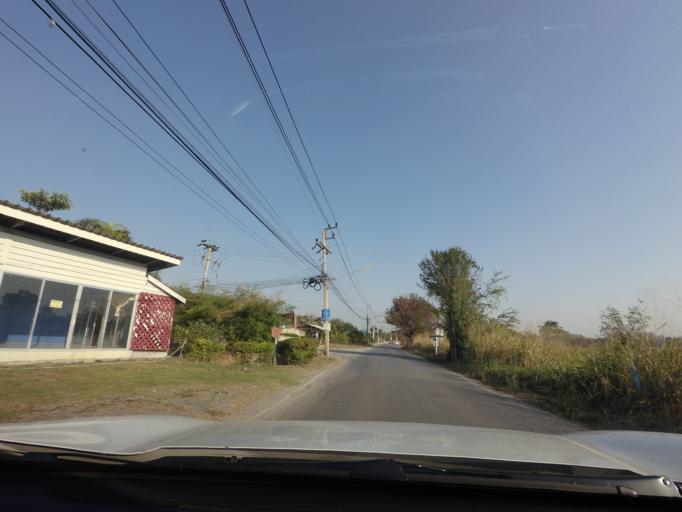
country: TH
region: Nakhon Ratchasima
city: Pak Chong
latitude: 14.6009
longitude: 101.4444
